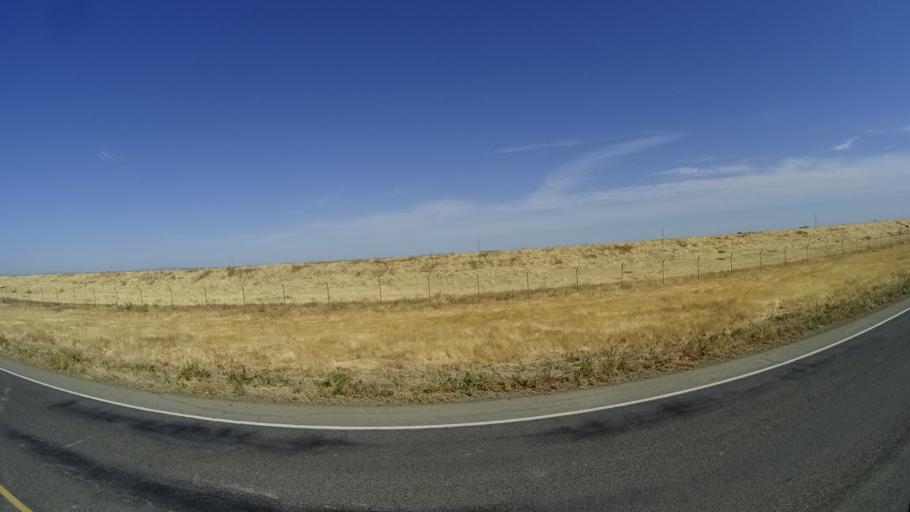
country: US
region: California
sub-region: Kings County
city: Lemoore Station
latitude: 36.2395
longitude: -119.8813
